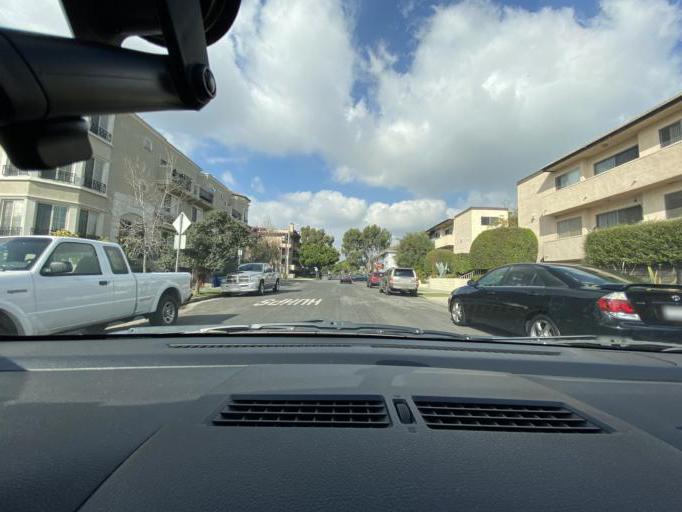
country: US
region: California
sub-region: Los Angeles County
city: Culver City
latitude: 34.0200
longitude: -118.4196
